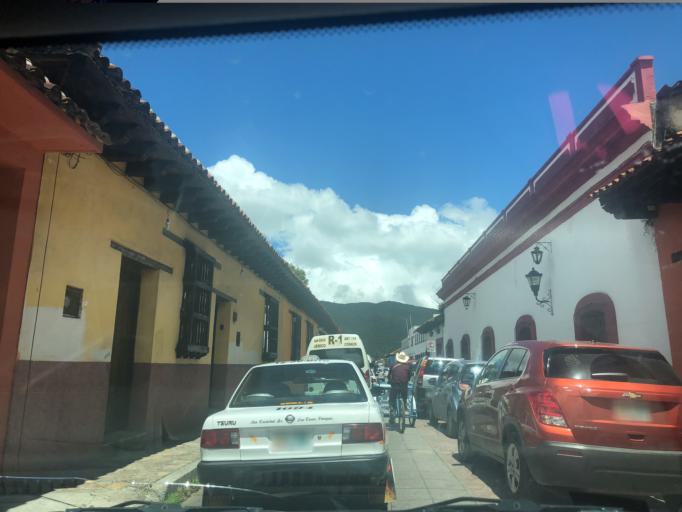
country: MX
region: Chiapas
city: San Cristobal de las Casas
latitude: 16.7346
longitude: -92.6389
